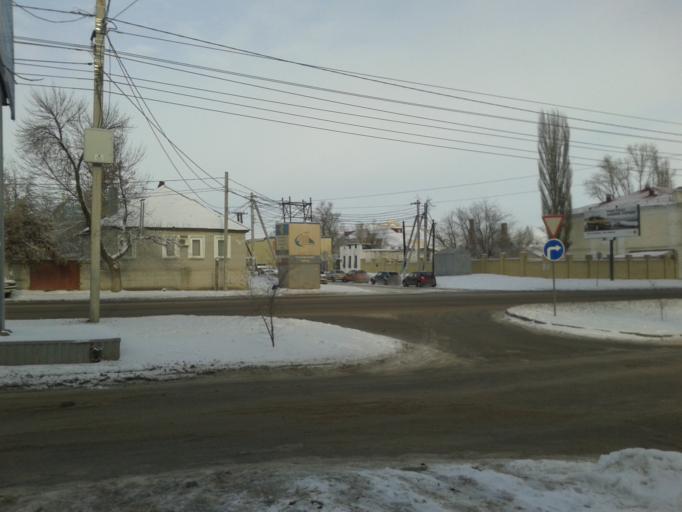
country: RU
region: Volgograd
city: Volgograd
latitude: 48.7246
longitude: 44.5155
